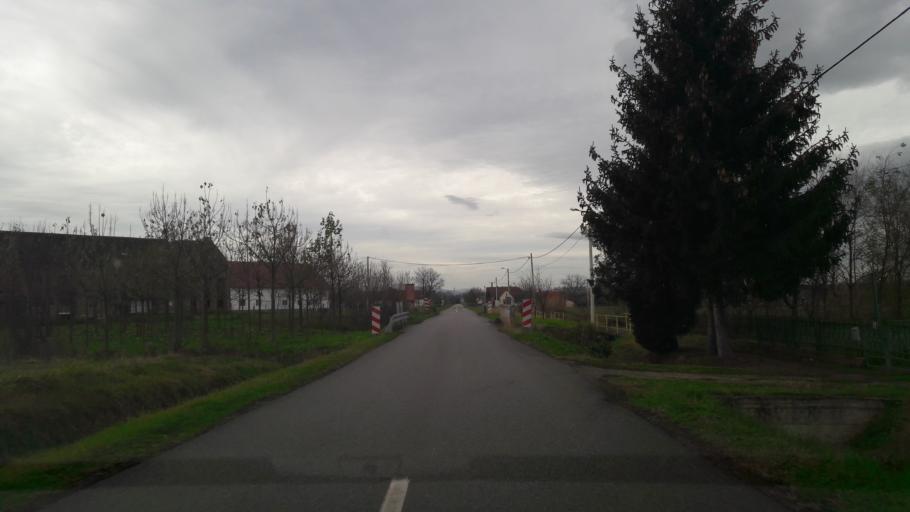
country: HR
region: Osjecko-Baranjska
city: Martin
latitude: 45.5308
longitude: 18.0469
